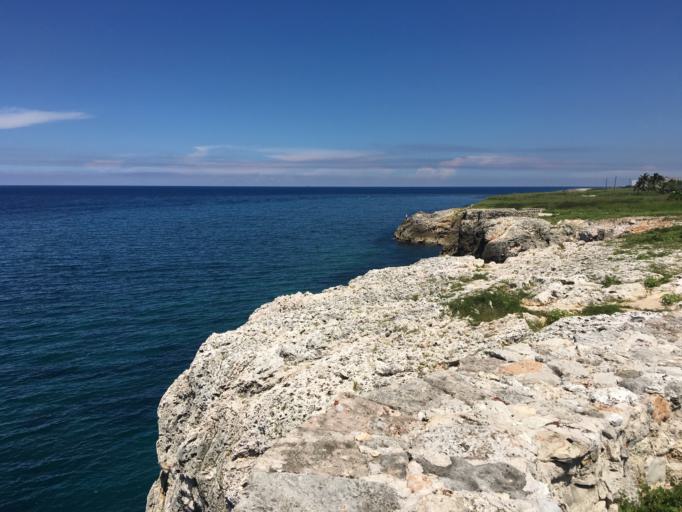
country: CU
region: La Habana
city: Centro Habana
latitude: 23.1519
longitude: -82.3559
